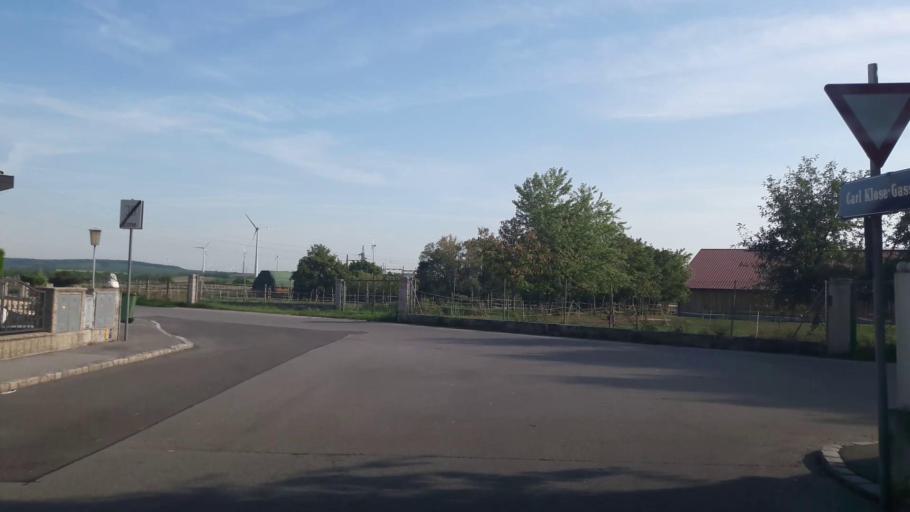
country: AT
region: Lower Austria
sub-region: Politischer Bezirk Bruck an der Leitha
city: Bruck an der Leitha
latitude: 48.0311
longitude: 16.7663
